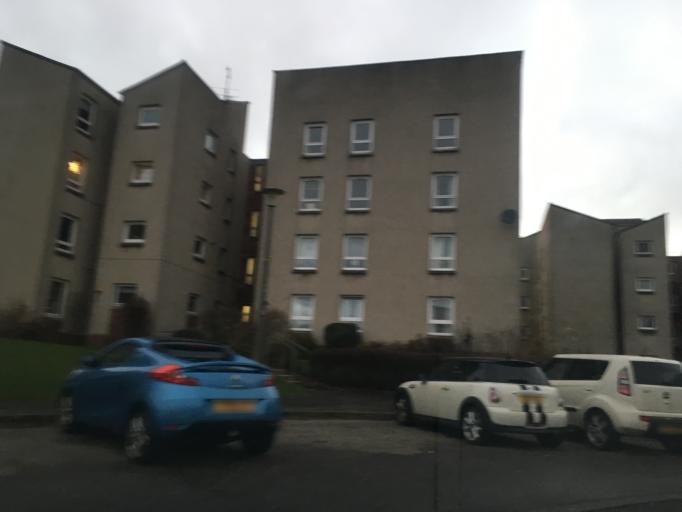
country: GB
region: Scotland
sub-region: Edinburgh
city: Colinton
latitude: 55.9194
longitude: -3.2667
